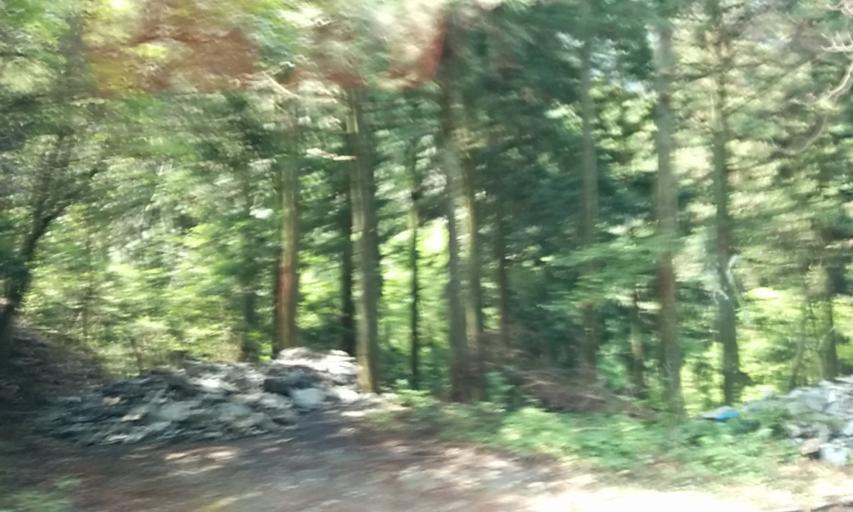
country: JP
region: Ehime
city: Niihama
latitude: 33.8678
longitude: 133.2956
